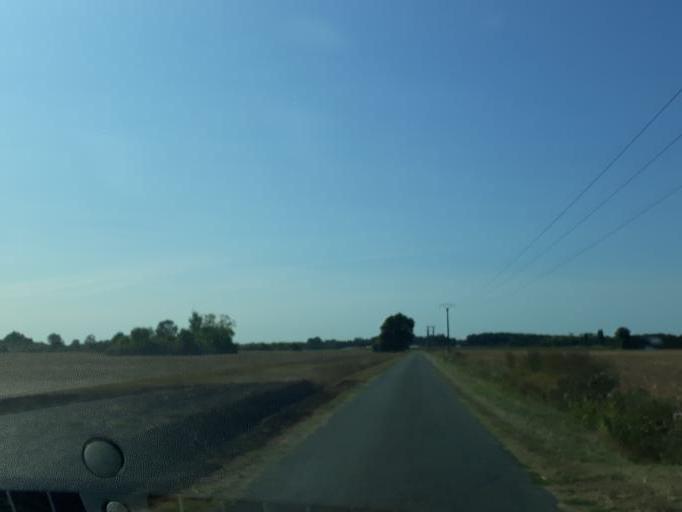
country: FR
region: Centre
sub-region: Departement du Loir-et-Cher
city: Selles-sur-Cher
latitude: 47.2678
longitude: 1.5891
